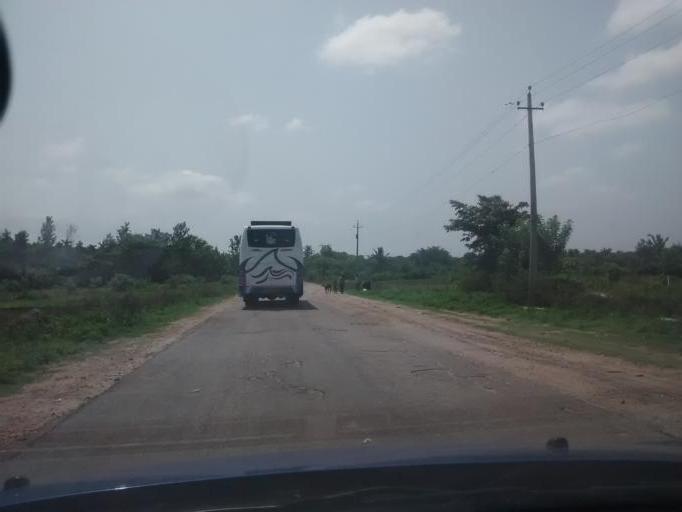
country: IN
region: Karnataka
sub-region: Hassan
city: Konanur
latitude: 12.5819
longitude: 76.1800
